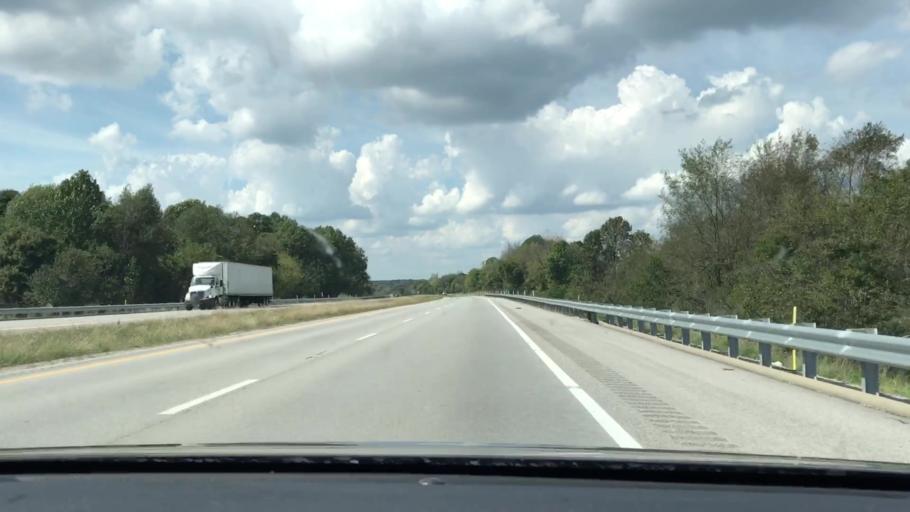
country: US
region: Kentucky
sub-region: Barren County
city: Glasgow
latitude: 37.0046
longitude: -86.0045
